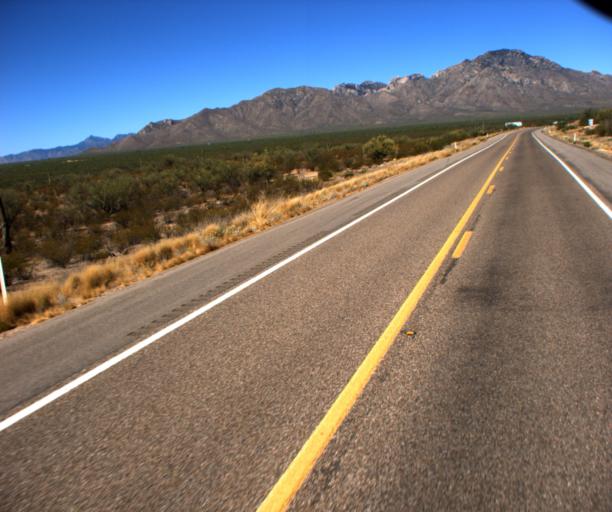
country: US
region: Arizona
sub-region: Pima County
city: Three Points
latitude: 32.0435
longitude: -111.4381
